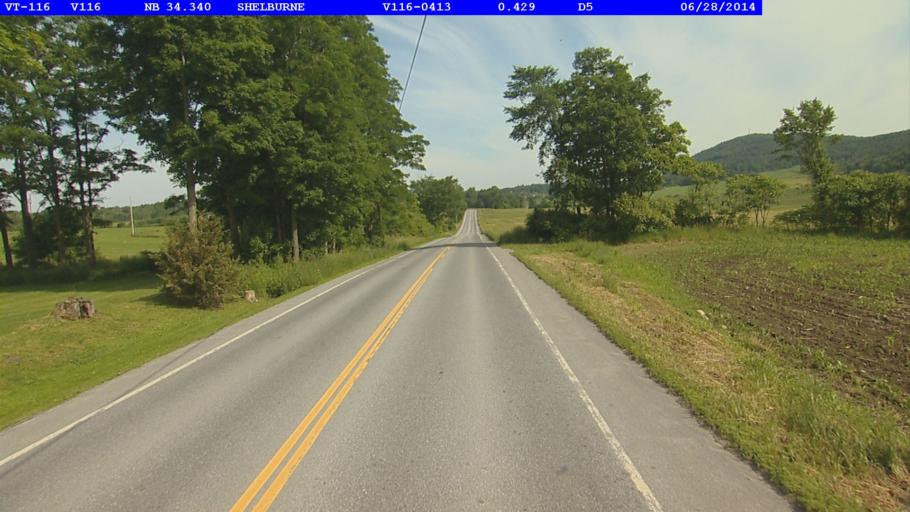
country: US
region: Vermont
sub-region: Chittenden County
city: Hinesburg
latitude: 44.3852
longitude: -73.1404
